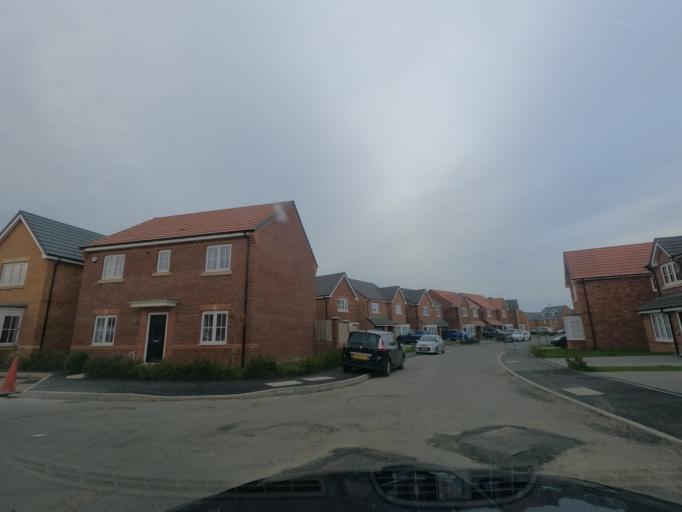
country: GB
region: England
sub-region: Northumberland
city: Seghill
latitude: 55.0770
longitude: -1.5627
